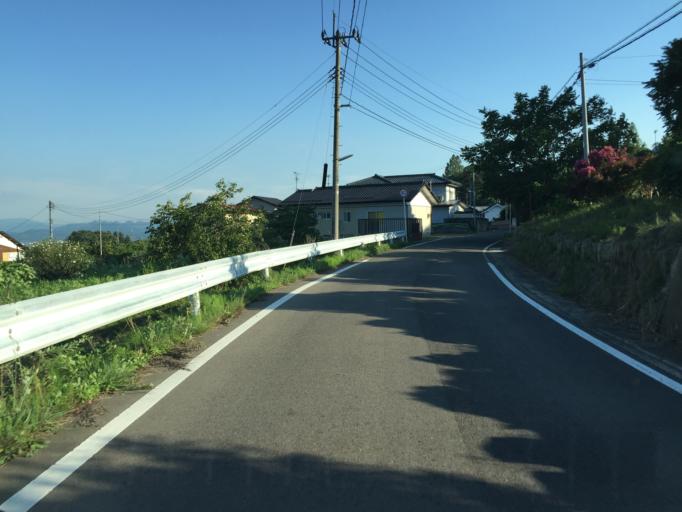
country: JP
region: Fukushima
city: Hobaramachi
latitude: 37.8776
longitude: 140.5191
